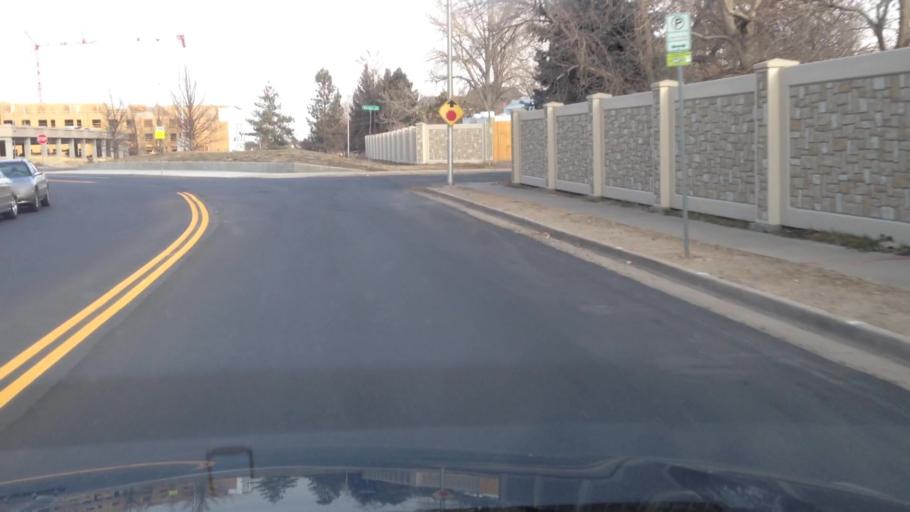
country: US
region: Colorado
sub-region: Adams County
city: Aurora
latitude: 39.6712
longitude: -104.8240
